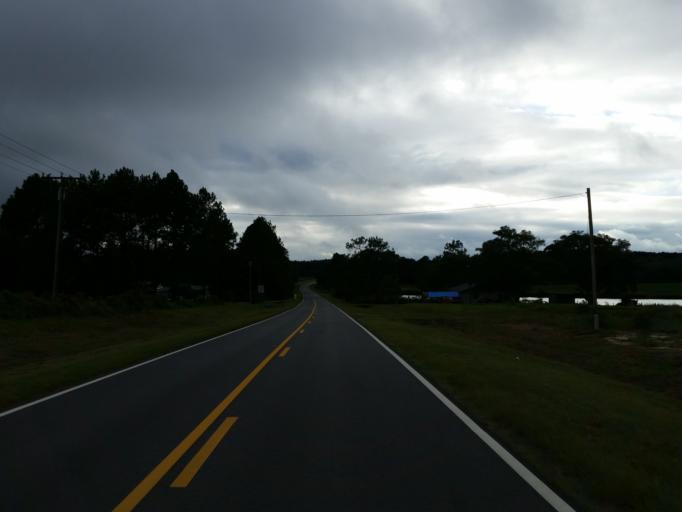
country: US
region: Georgia
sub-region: Tift County
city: Tifton
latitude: 31.5699
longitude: -83.5550
